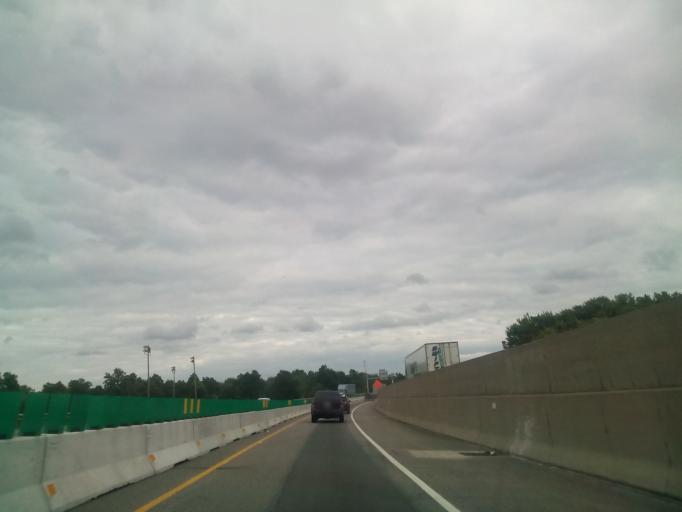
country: US
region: Ohio
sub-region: Lorain County
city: Elyria
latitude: 41.3858
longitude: -82.0743
